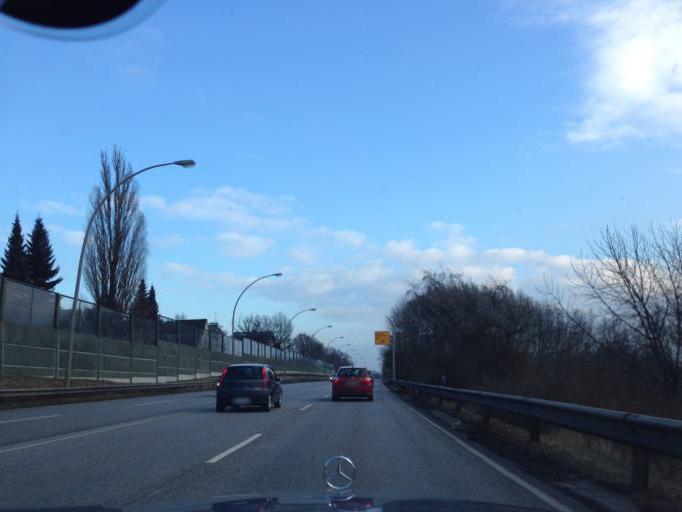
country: DE
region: Schleswig-Holstein
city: Oststeinbek
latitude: 53.5251
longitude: 10.1394
